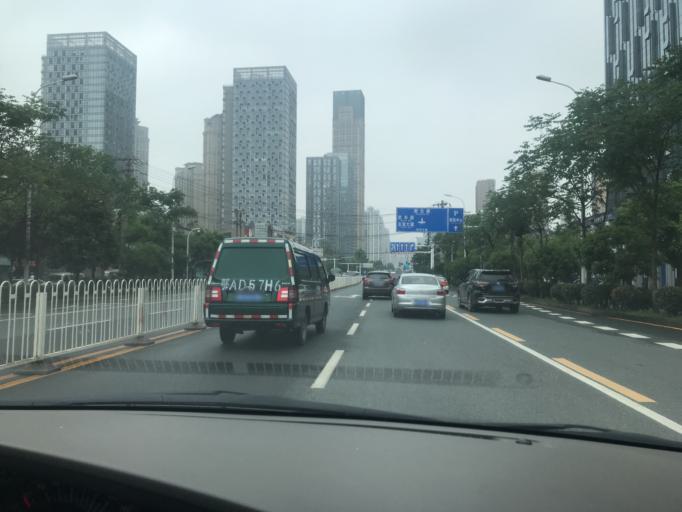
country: CN
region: Hubei
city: Jiang'an
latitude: 30.5808
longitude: 114.3174
